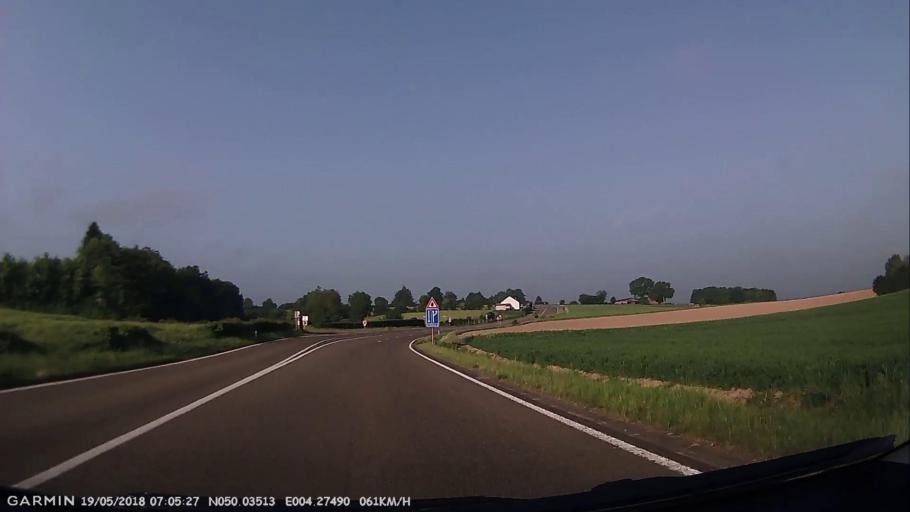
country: BE
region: Wallonia
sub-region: Province du Hainaut
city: Chimay
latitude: 50.0350
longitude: 4.2748
